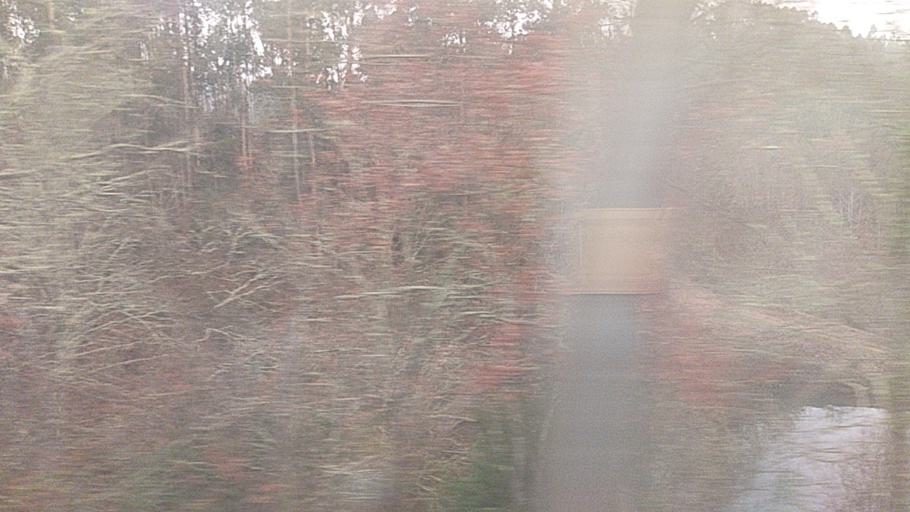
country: PT
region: Viseu
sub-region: Mortagua
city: Mortagua
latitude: 40.4094
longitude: -8.3123
